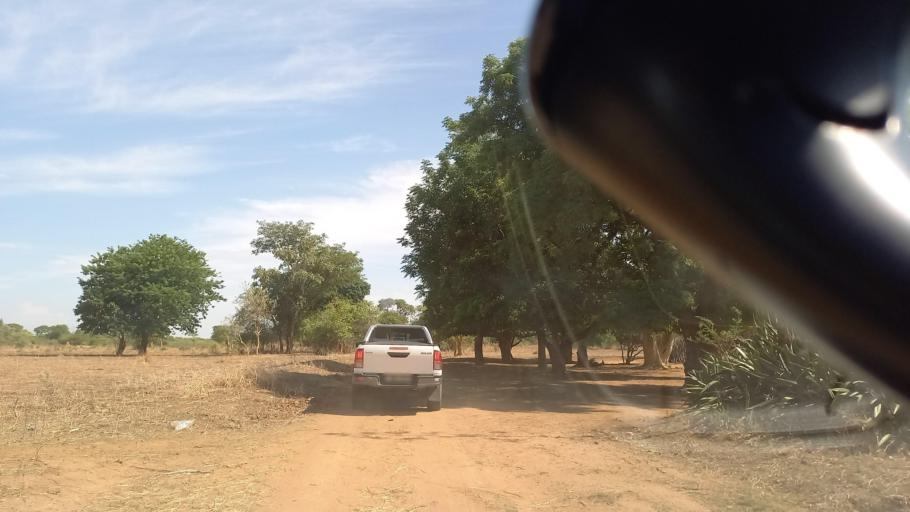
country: ZM
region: Southern
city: Mazabuka
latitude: -16.0355
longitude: 27.6230
